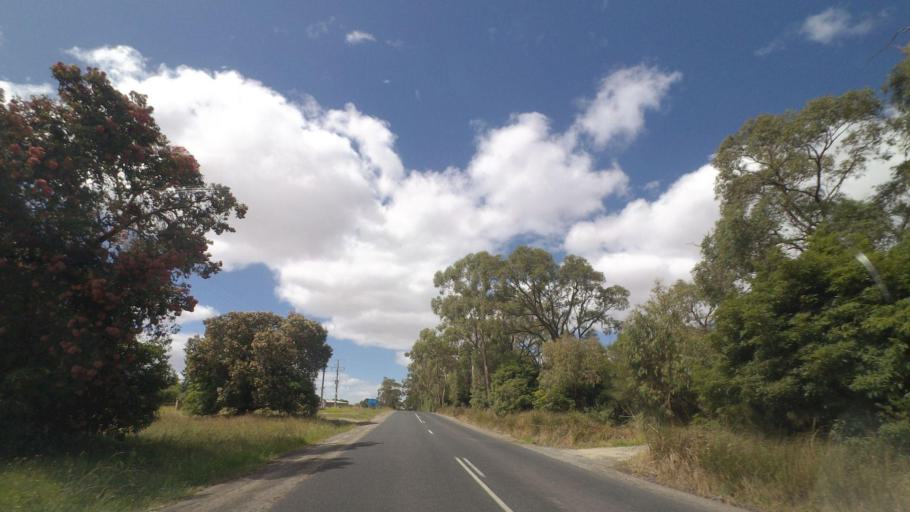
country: AU
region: Victoria
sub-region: Cardinia
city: Koo-Wee-Rup
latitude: -38.3177
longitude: 145.6682
